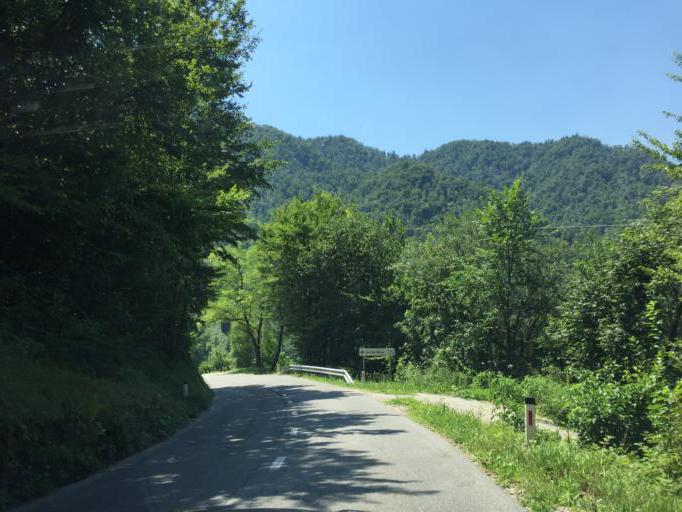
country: SI
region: Idrija
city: Spodnja Idrija
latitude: 46.0284
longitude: 14.0297
